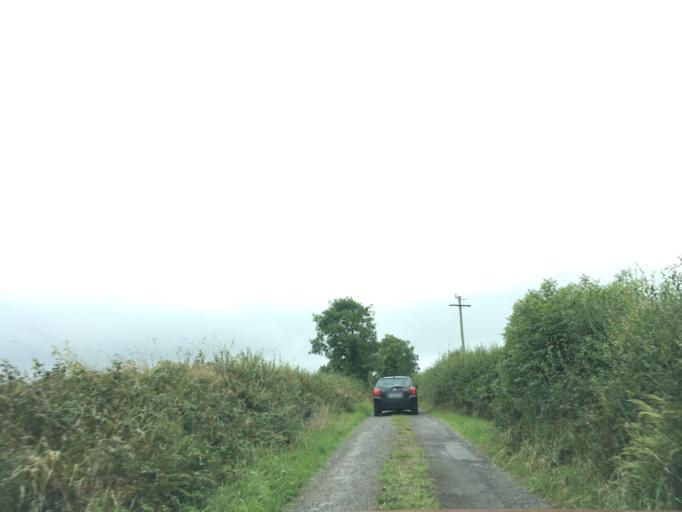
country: IE
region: Munster
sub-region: An Clar
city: Ennis
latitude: 52.7235
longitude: -9.0953
